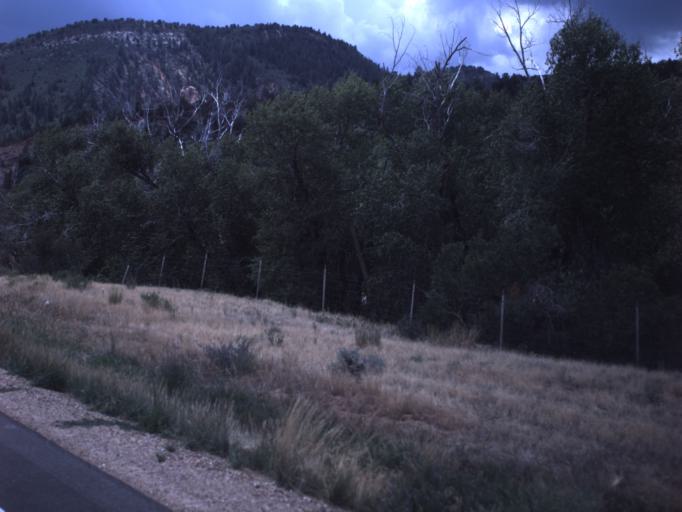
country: US
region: Utah
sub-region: Duchesne County
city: Duchesne
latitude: 40.4284
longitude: -110.8020
